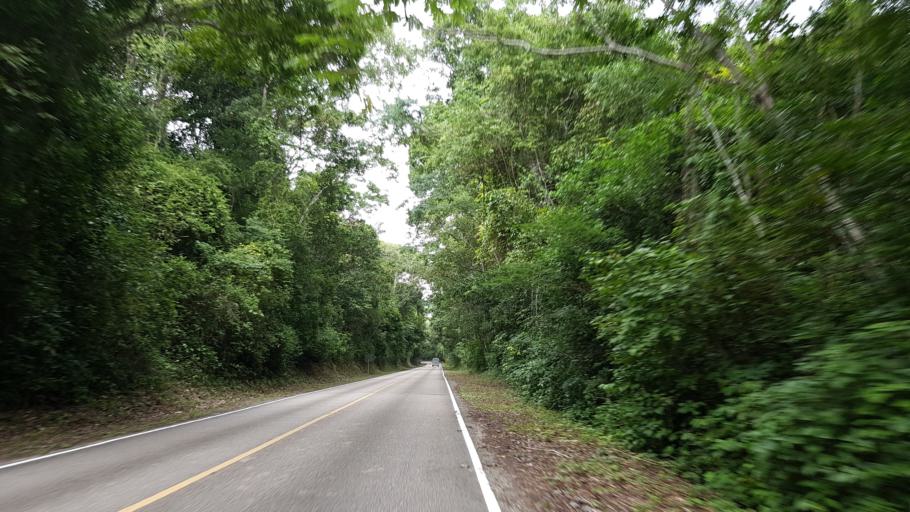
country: GT
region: Peten
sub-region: Municipio de San Jose
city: San Jose
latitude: 17.2116
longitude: -89.6146
